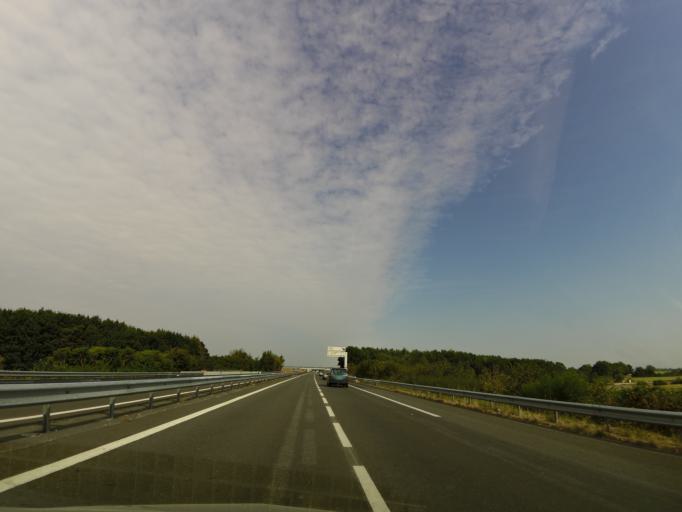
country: FR
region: Pays de la Loire
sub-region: Departement de la Loire-Atlantique
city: Aigrefeuille-sur-Maine
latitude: 47.0676
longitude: -1.4335
